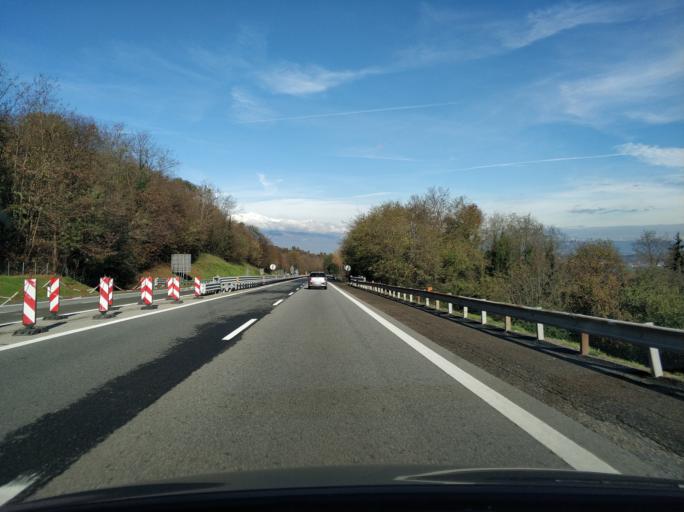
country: IT
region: Piedmont
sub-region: Provincia di Torino
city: Cuceglio
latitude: 45.3631
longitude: 7.8365
